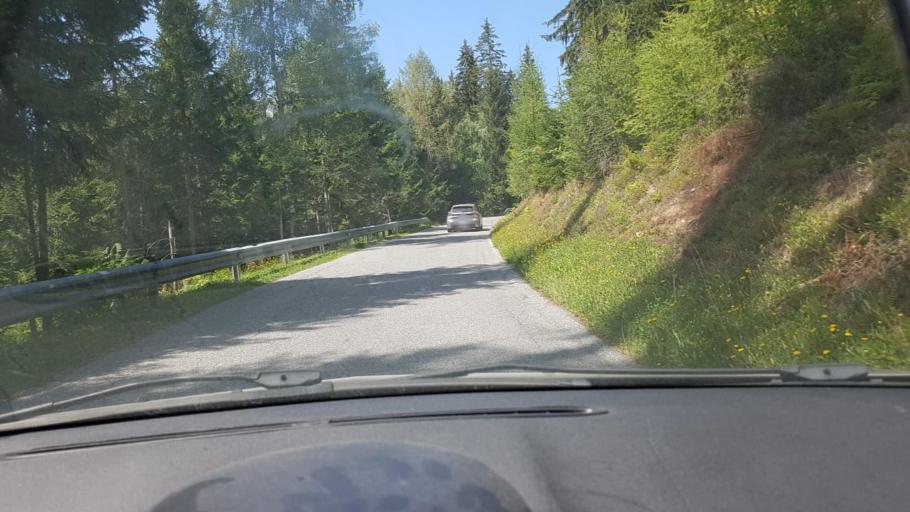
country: AT
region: Carinthia
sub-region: Politischer Bezirk Volkermarkt
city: Bad Eisenkappel
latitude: 46.4264
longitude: 14.5930
